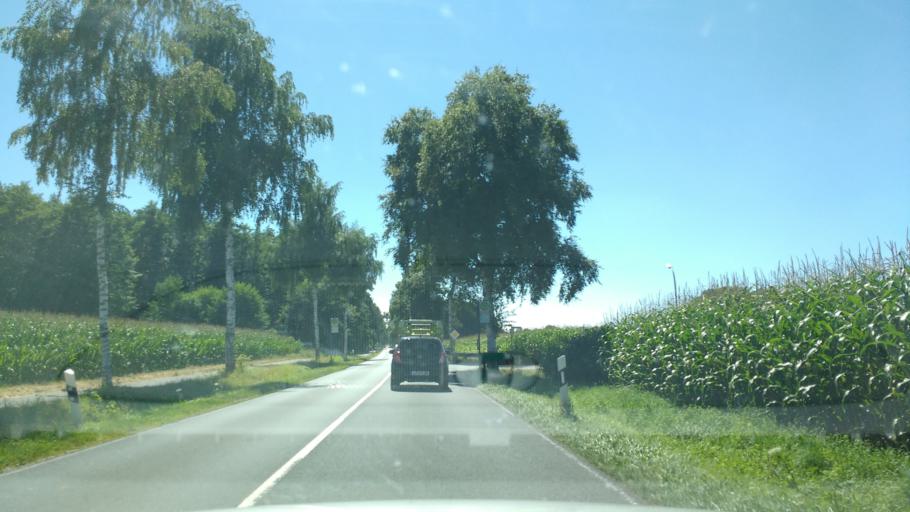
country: DE
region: North Rhine-Westphalia
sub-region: Regierungsbezirk Arnsberg
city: Lippstadt
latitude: 51.7025
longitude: 8.4185
